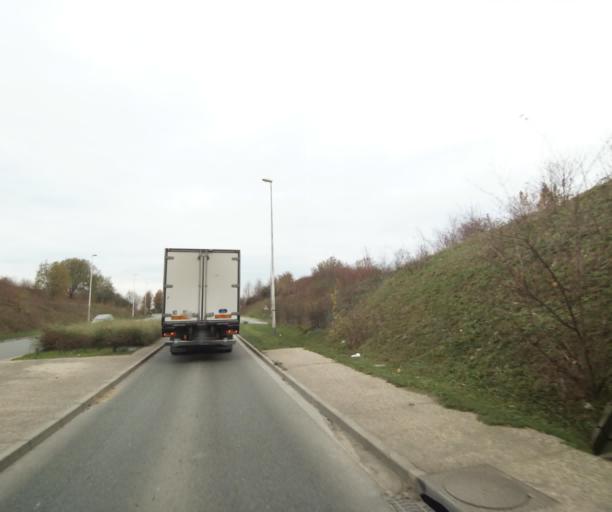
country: FR
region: Ile-de-France
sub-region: Departement du Val-d'Oise
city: Le Thillay
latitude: 49.0104
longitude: 2.4911
